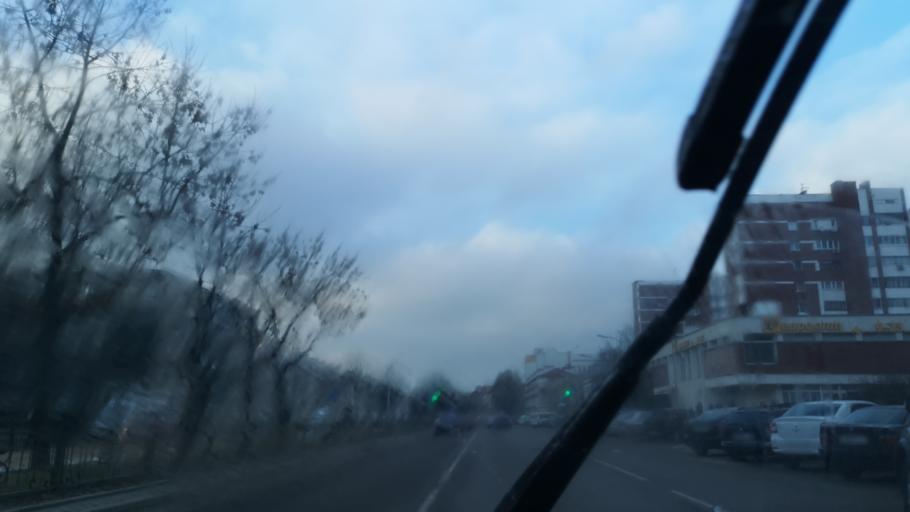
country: BY
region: Brest
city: Brest
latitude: 52.0911
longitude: 23.7013
